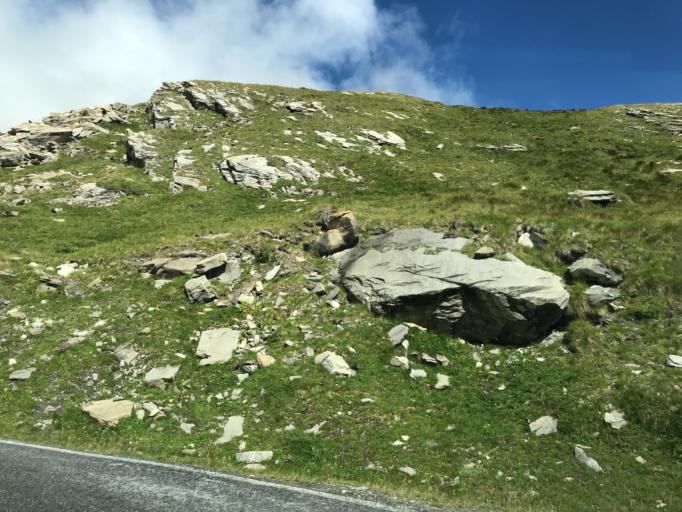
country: IT
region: Piedmont
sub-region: Provincia di Cuneo
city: Pontechianale
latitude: 44.6709
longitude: 6.9880
